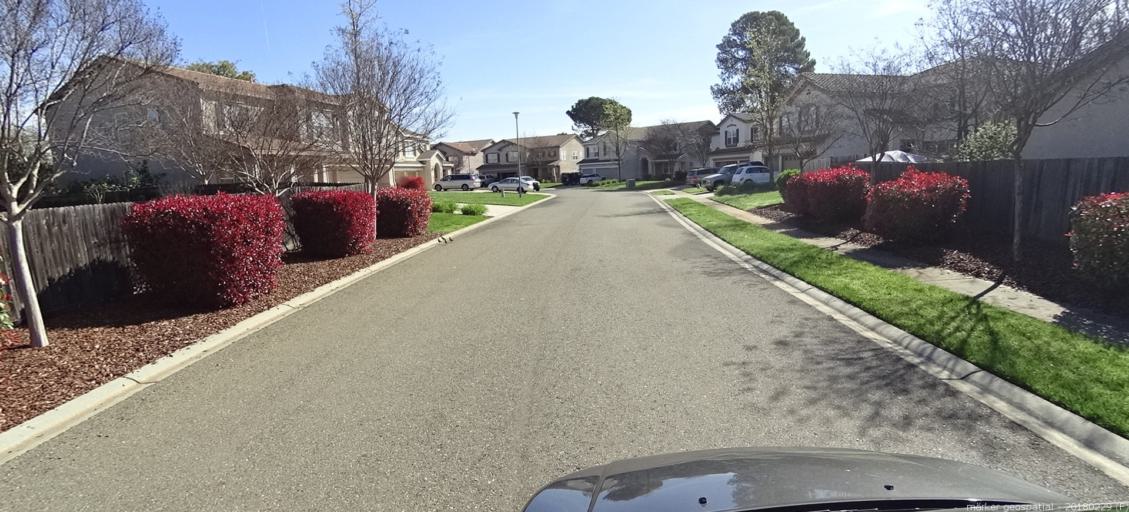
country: US
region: California
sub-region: Sacramento County
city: Rancho Cordova
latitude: 38.5417
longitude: -121.2703
